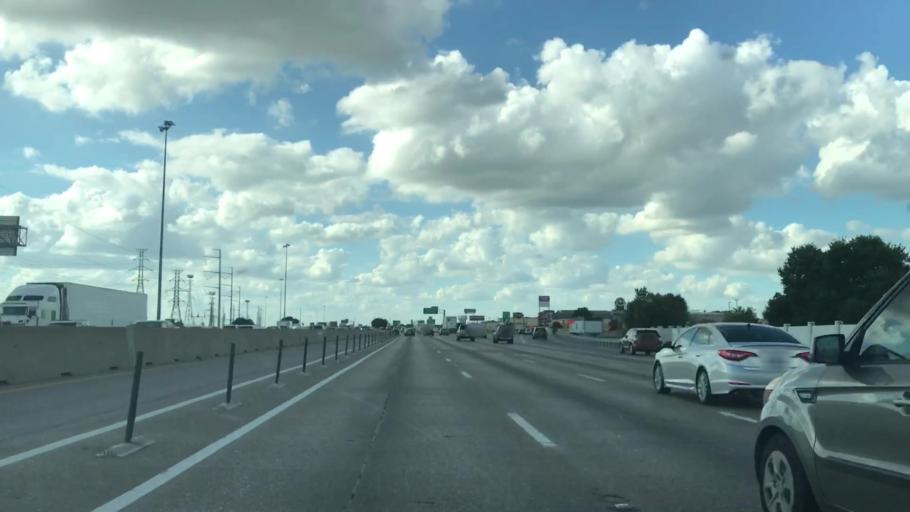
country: US
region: Texas
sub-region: Dallas County
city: Garland
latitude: 32.8523
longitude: -96.6436
